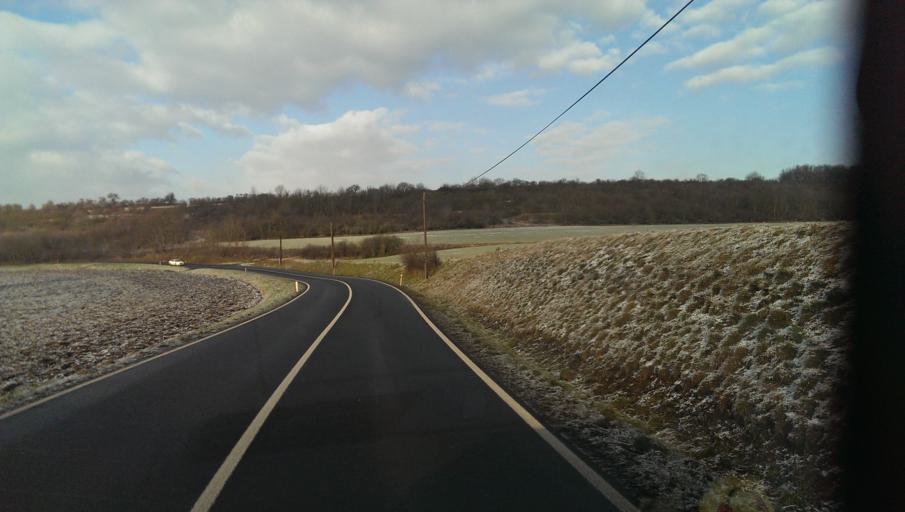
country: CZ
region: Ustecky
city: Budyne nad Ohri
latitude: 50.4129
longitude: 14.1093
